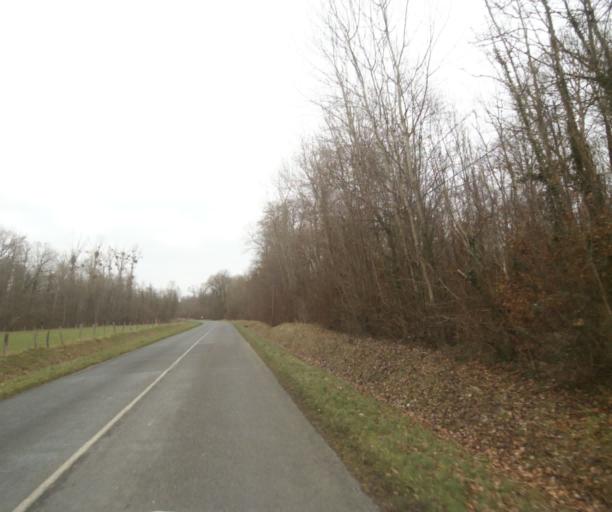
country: FR
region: Champagne-Ardenne
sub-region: Departement de la Haute-Marne
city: Villiers-en-Lieu
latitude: 48.6875
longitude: 4.8870
